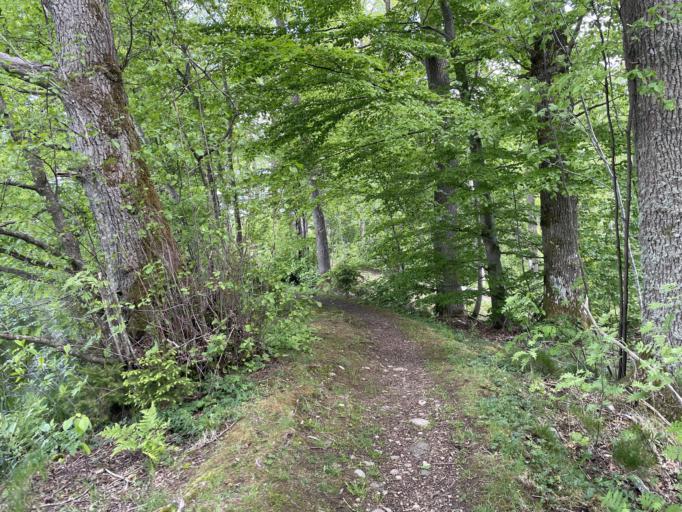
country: SE
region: Skane
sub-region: Klippans Kommun
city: Klippan
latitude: 56.1599
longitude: 13.1551
